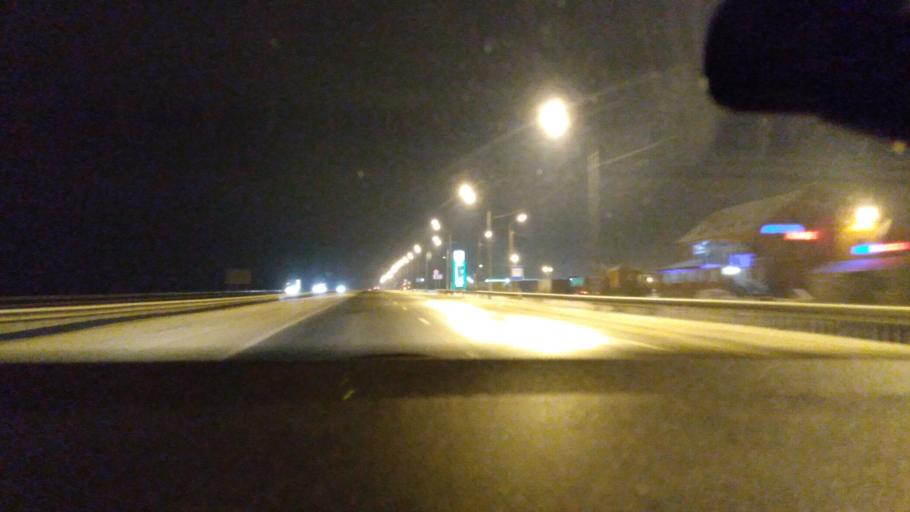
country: RU
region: Moskovskaya
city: Kolomna
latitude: 55.1201
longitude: 38.8224
